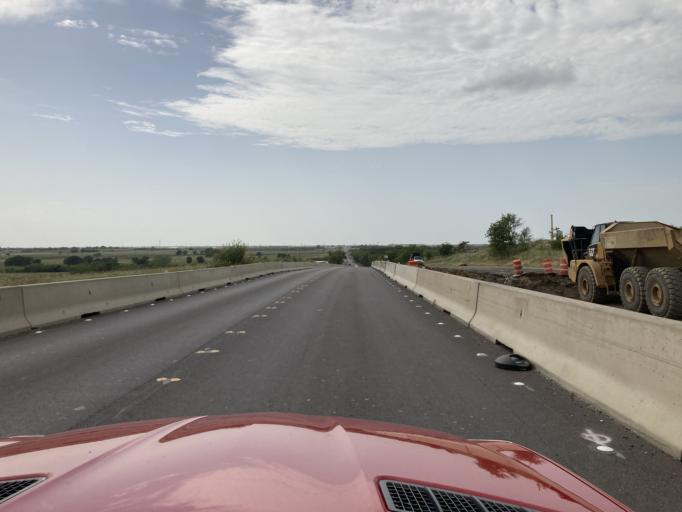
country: US
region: Texas
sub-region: Navarro County
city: Corsicana
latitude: 32.0502
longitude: -96.4209
